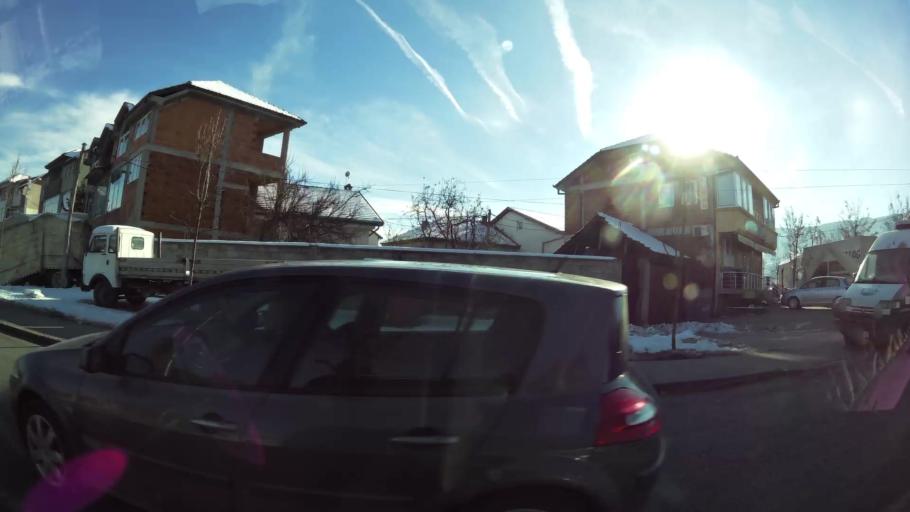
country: MK
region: Saraj
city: Saraj
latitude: 42.0023
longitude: 21.3311
